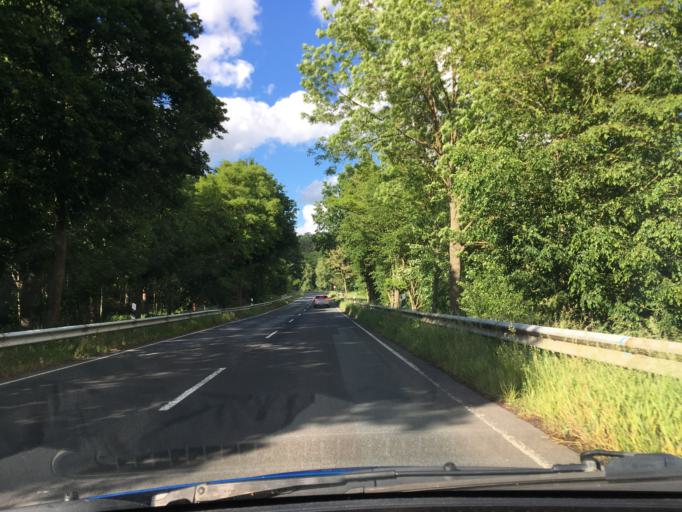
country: DE
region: Lower Saxony
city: Moringen
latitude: 51.7177
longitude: 9.8768
